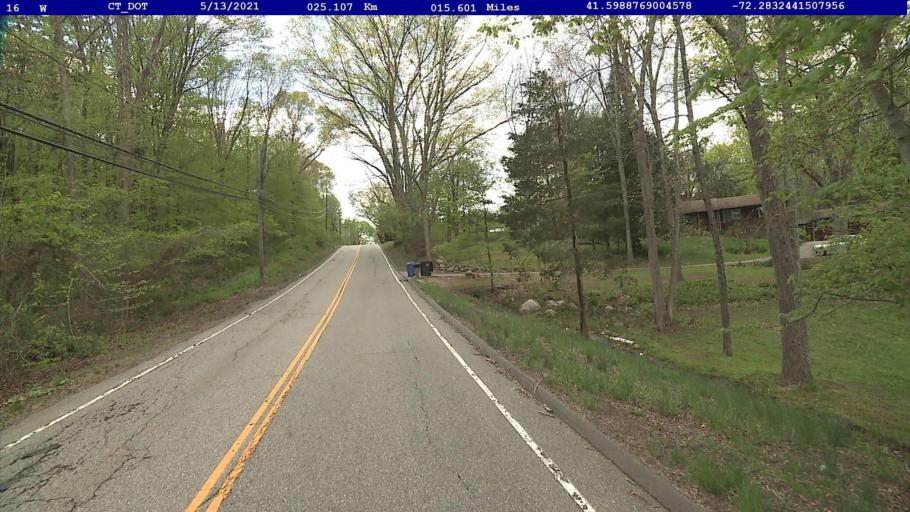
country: US
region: Connecticut
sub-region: New London County
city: Colchester
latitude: 41.5989
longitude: -72.2832
